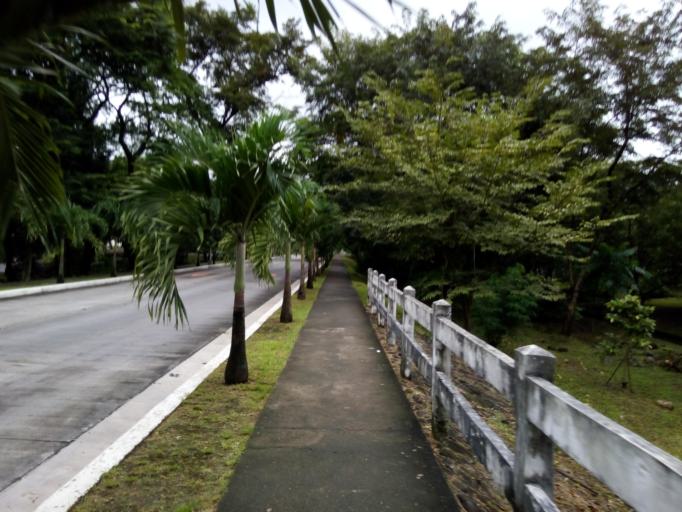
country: PH
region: Metro Manila
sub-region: Quezon City
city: Quezon City
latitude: 14.6498
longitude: 121.0699
